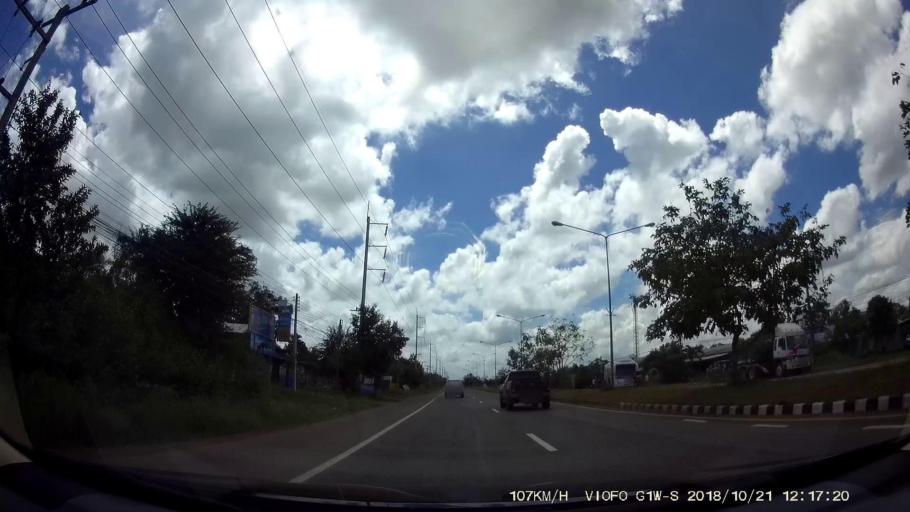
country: TH
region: Nakhon Ratchasima
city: Dan Khun Thot
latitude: 15.3335
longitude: 101.8210
